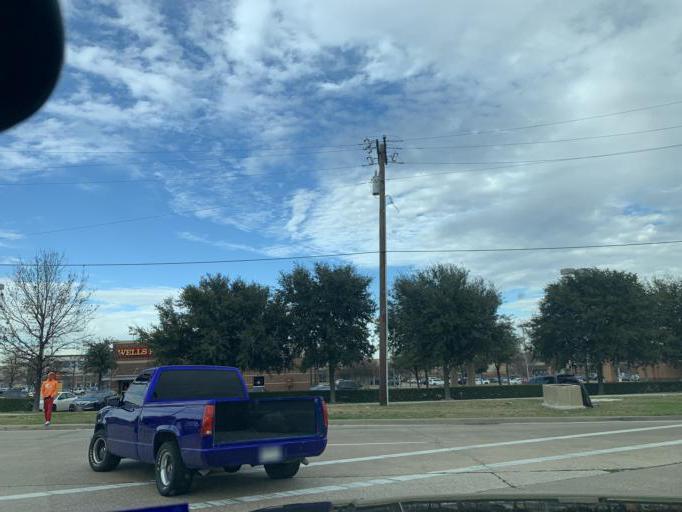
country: US
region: Texas
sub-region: Dallas County
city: Duncanville
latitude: 32.6476
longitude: -96.8615
